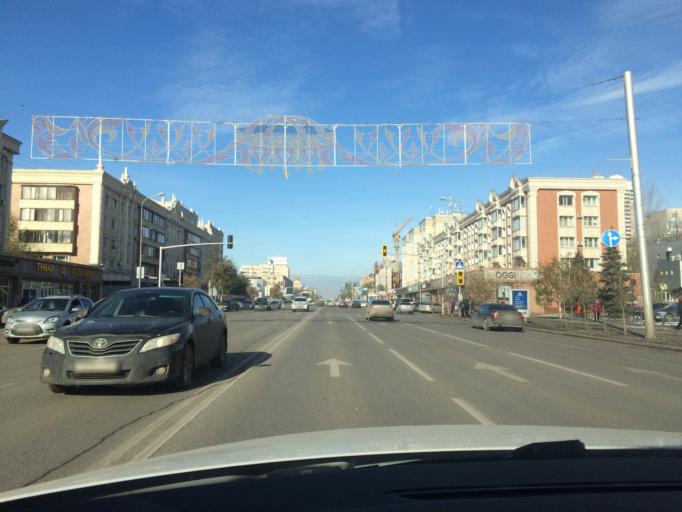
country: KZ
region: Astana Qalasy
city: Astana
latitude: 51.1602
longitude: 71.4289
